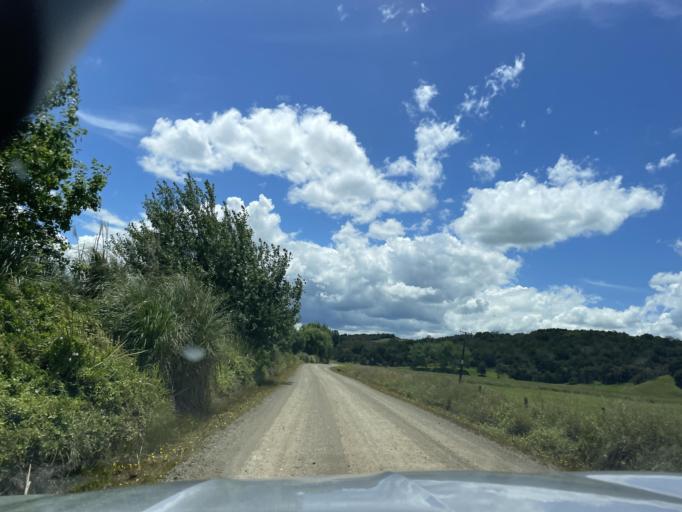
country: NZ
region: Northland
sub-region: Kaipara District
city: Dargaville
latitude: -35.9014
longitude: 173.9206
